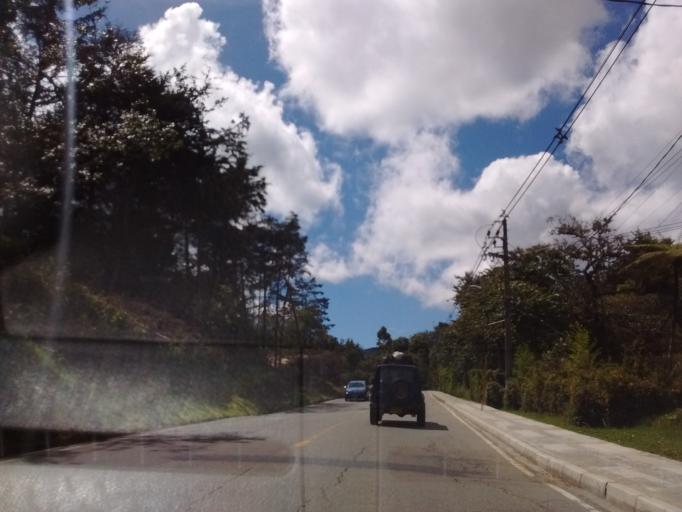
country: CO
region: Antioquia
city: Medellin
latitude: 6.2117
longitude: -75.5012
